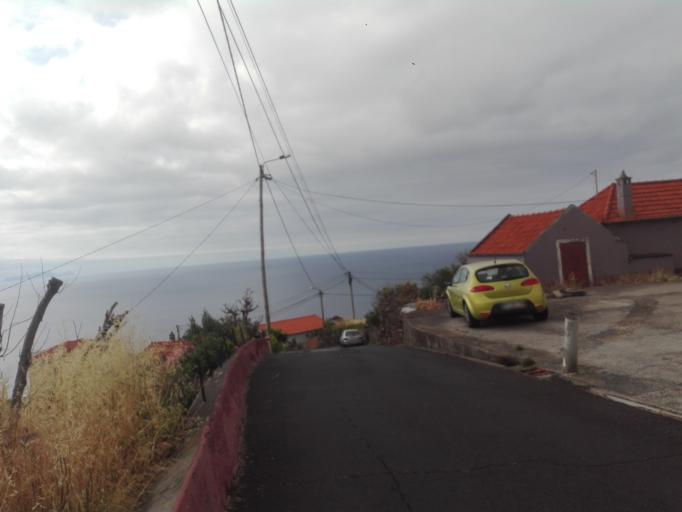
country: PT
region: Madeira
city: Canico
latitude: 32.6529
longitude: -16.8277
